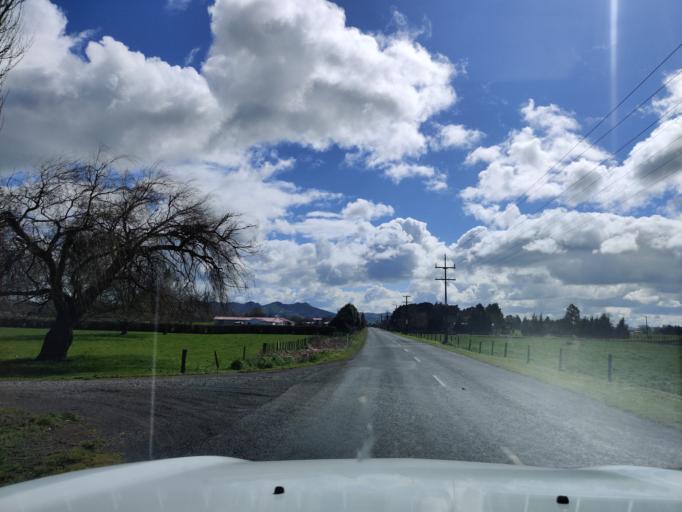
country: NZ
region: Waikato
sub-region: Waikato District
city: Ngaruawahia
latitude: -37.5754
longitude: 175.2683
